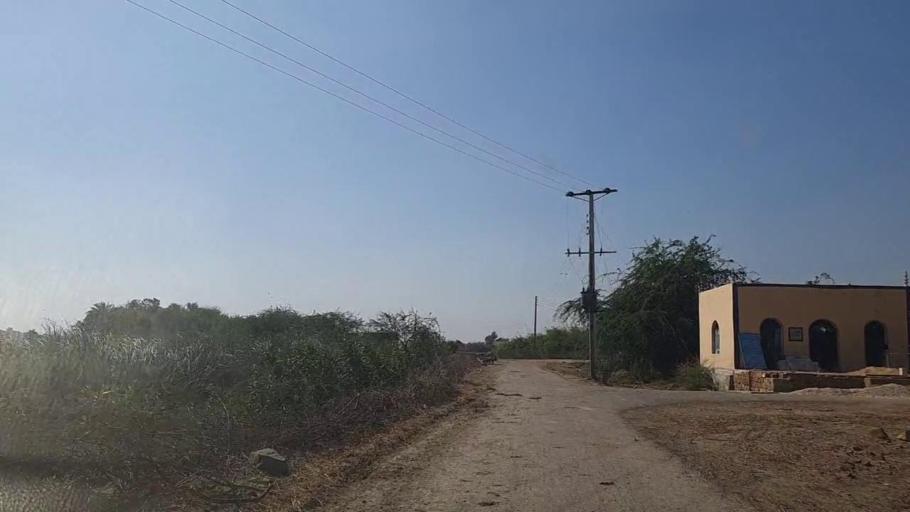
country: PK
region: Sindh
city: Daro Mehar
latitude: 24.9738
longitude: 68.1243
